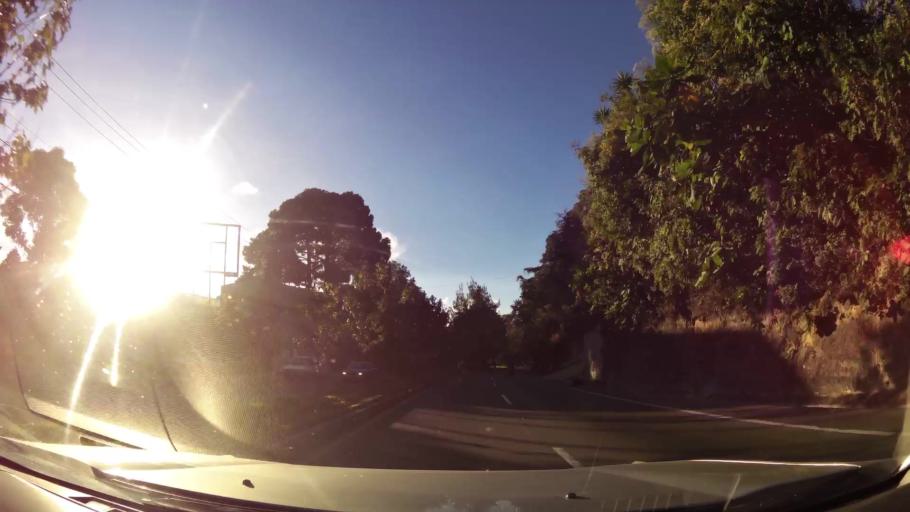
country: GT
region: Sacatepequez
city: San Lucas Sacatepequez
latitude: 14.5996
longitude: -90.6406
